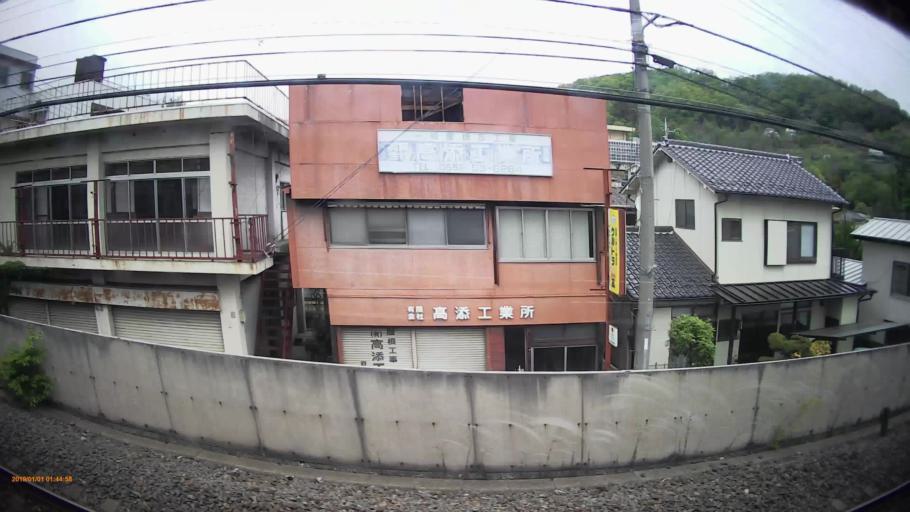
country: JP
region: Yamanashi
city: Kofu-shi
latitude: 35.6656
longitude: 138.5749
